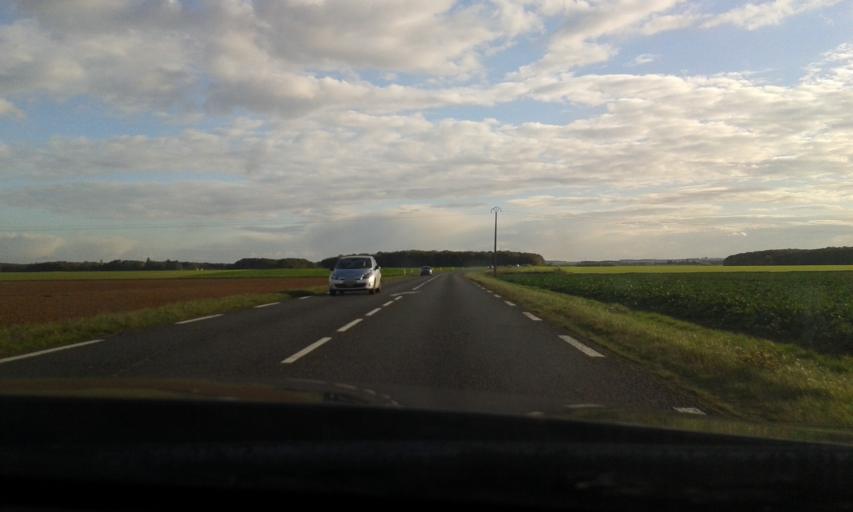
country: FR
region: Centre
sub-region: Departement d'Eure-et-Loir
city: Vernouillet
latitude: 48.6959
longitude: 1.3772
